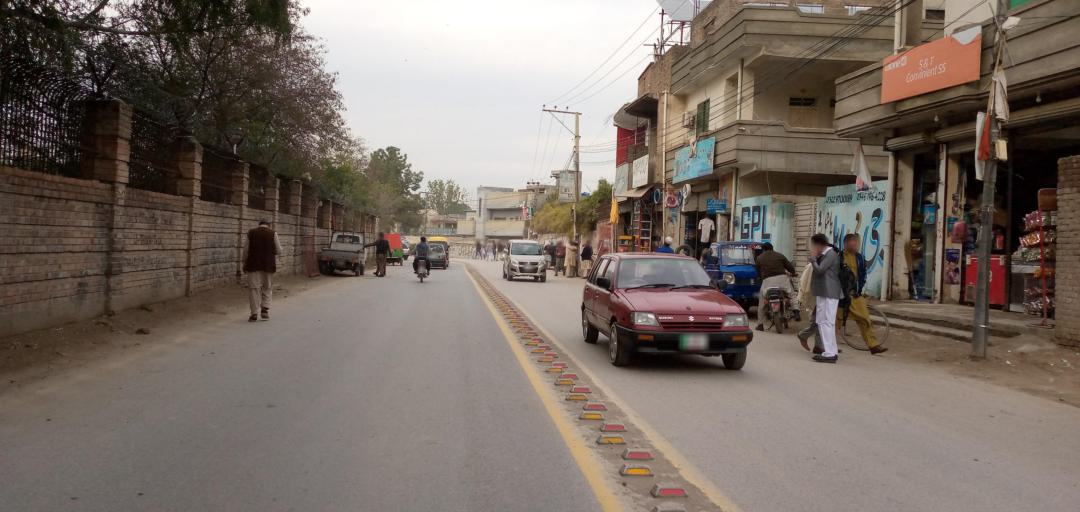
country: PK
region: Khyber Pakhtunkhwa
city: Peshawar
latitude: 34.0223
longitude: 71.4897
